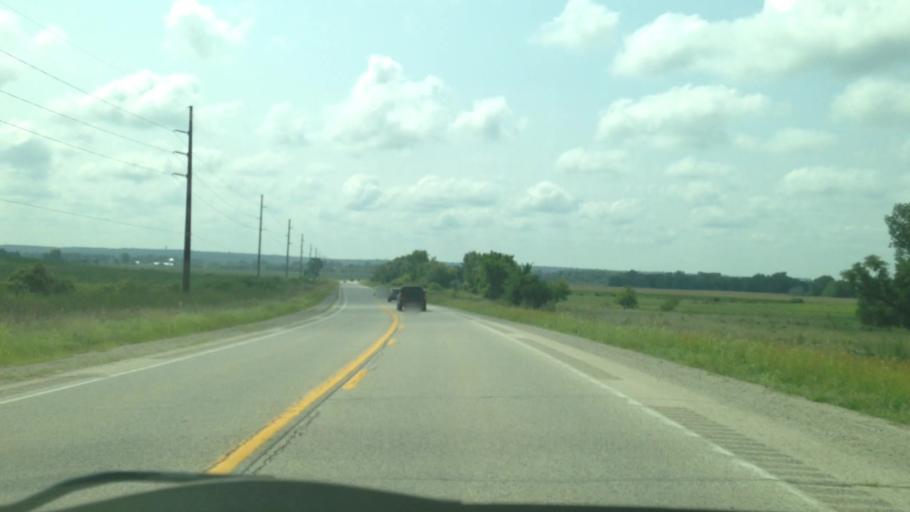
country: US
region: Iowa
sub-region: Benton County
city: Walford
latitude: 41.8218
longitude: -91.8731
